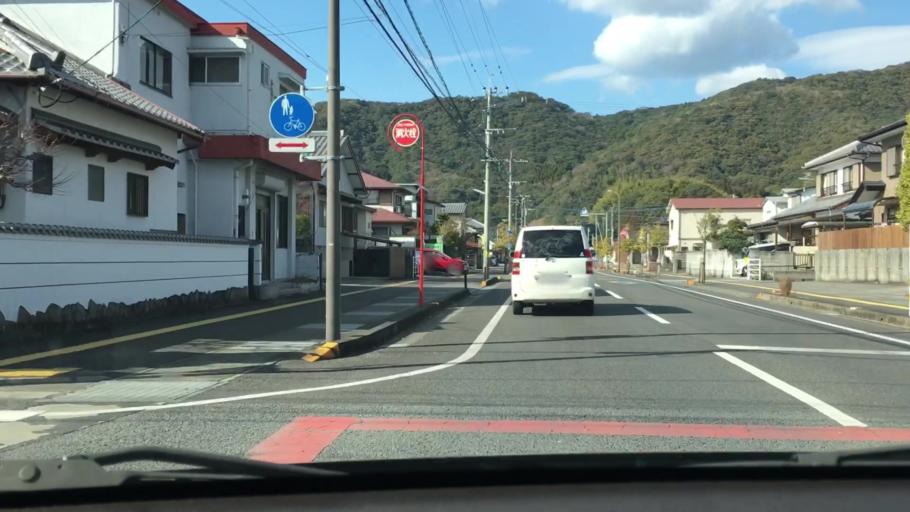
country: JP
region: Oita
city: Saiki
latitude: 32.9627
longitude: 131.8981
